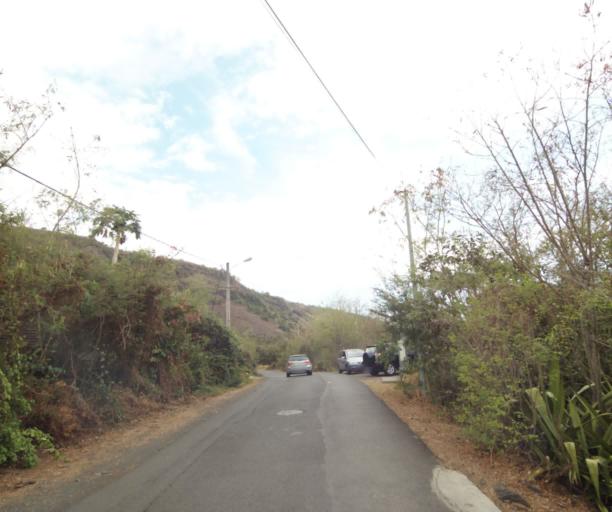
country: RE
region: Reunion
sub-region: Reunion
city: Saint-Paul
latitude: -21.0028
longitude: 55.3000
